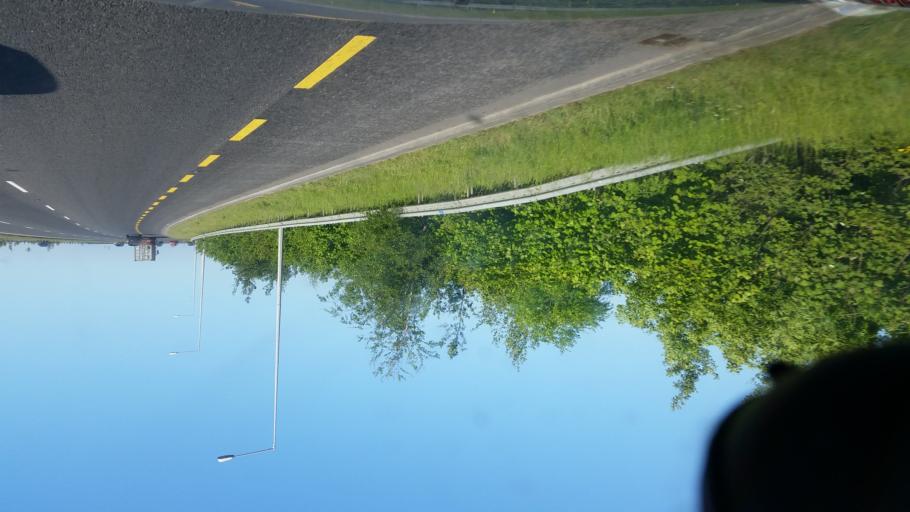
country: IE
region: Leinster
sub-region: Dublin City
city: Finglas
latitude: 53.4167
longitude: -6.3186
